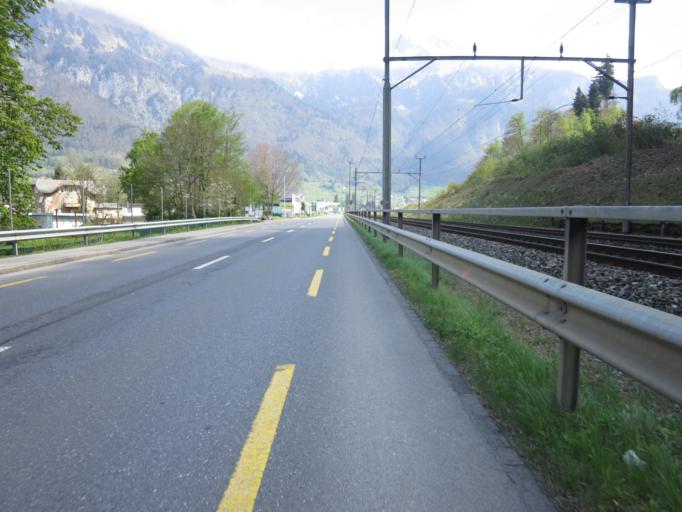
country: CH
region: Saint Gallen
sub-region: Wahlkreis Sarganserland
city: Walenstadt
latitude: 47.1163
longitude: 9.2999
